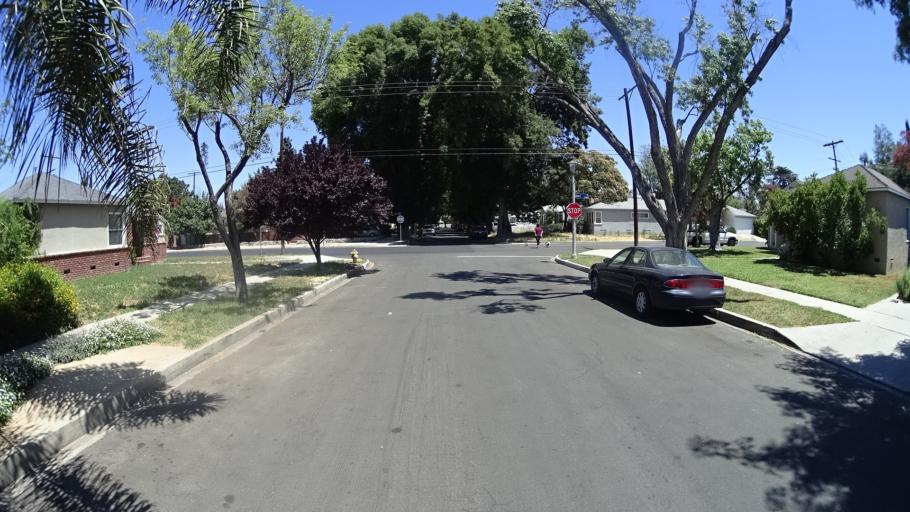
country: US
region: California
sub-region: Los Angeles County
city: Northridge
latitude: 34.1972
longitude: -118.5217
